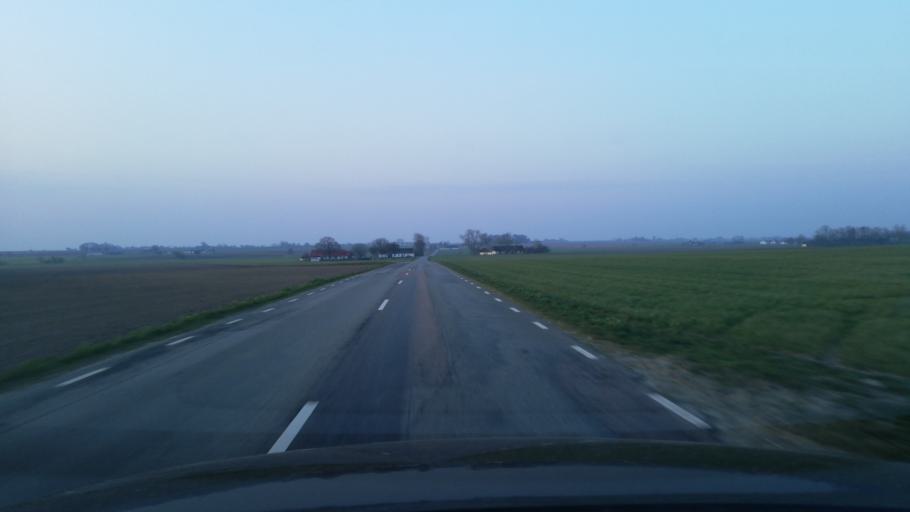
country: SE
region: Skane
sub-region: Tomelilla Kommun
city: Tomelilla
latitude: 55.4838
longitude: 14.1011
